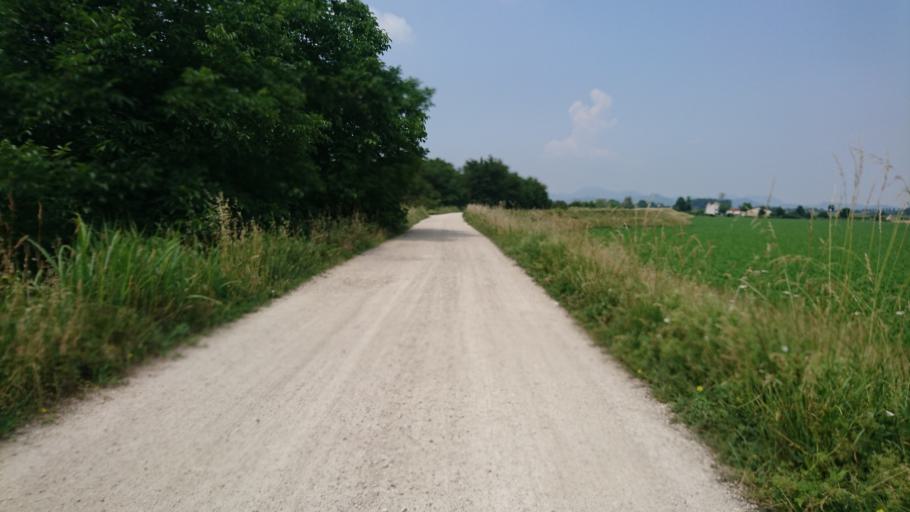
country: IT
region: Veneto
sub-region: Provincia di Padova
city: Bertipaglia
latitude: 45.2806
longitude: 11.8922
